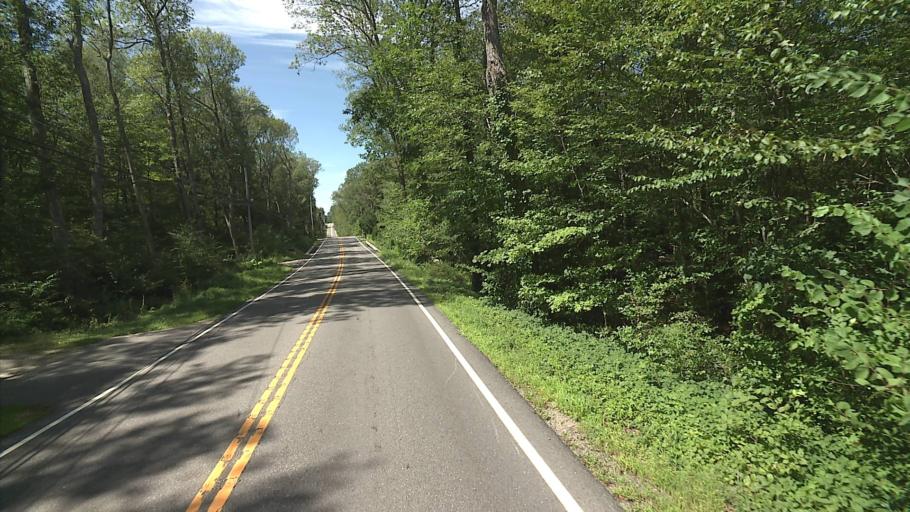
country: US
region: Connecticut
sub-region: Windham County
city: South Woodstock
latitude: 41.8957
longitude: -72.0537
